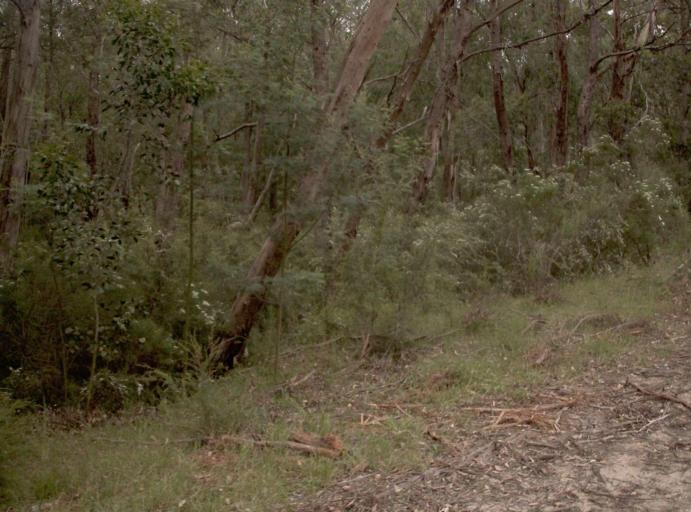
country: AU
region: Victoria
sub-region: East Gippsland
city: Bairnsdale
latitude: -37.7511
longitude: 147.5989
